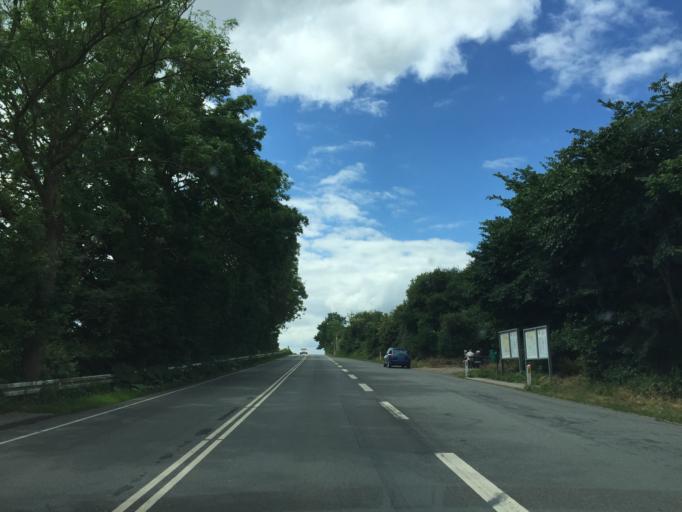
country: DK
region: South Denmark
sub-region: Svendborg Kommune
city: Svendborg
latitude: 55.0720
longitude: 10.5253
